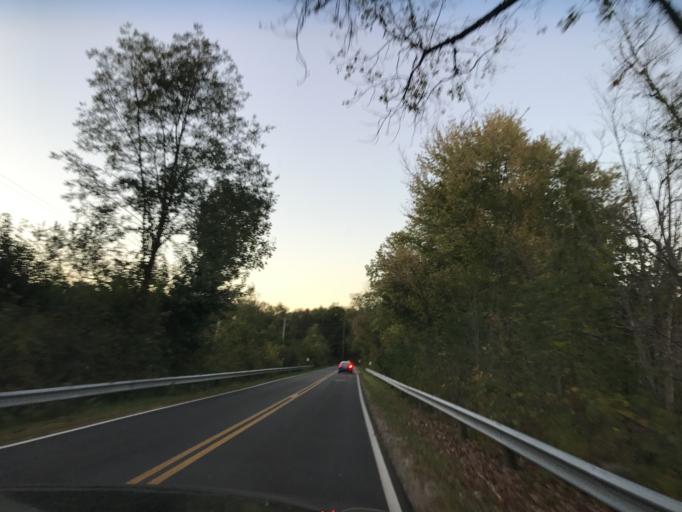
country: US
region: Ohio
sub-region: Delaware County
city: Sunbury
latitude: 40.2141
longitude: -82.8843
